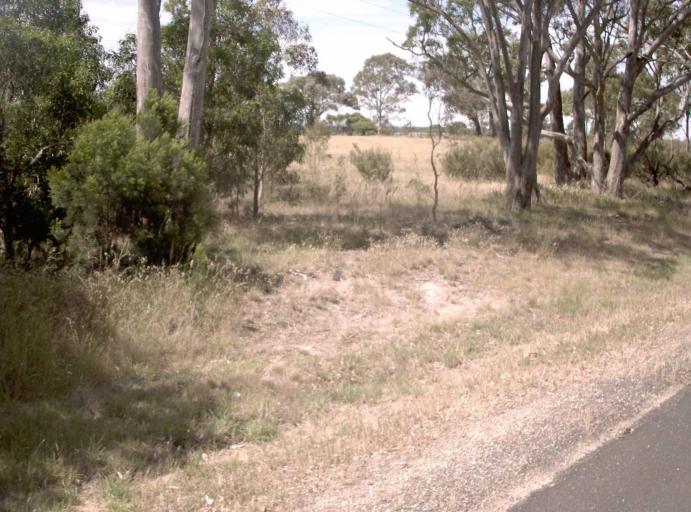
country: AU
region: Victoria
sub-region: Wellington
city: Sale
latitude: -37.9313
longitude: 147.1927
